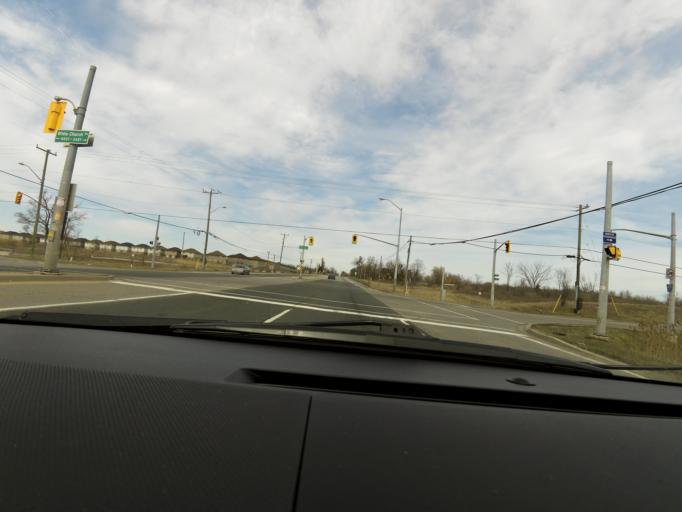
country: CA
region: Ontario
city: Ancaster
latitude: 43.1447
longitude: -79.9197
